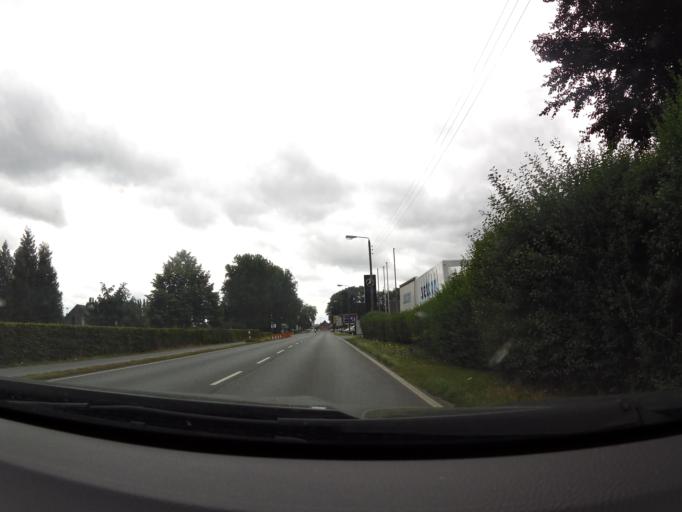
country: DE
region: North Rhine-Westphalia
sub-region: Regierungsbezirk Dusseldorf
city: Wesel
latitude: 51.6497
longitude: 6.6210
